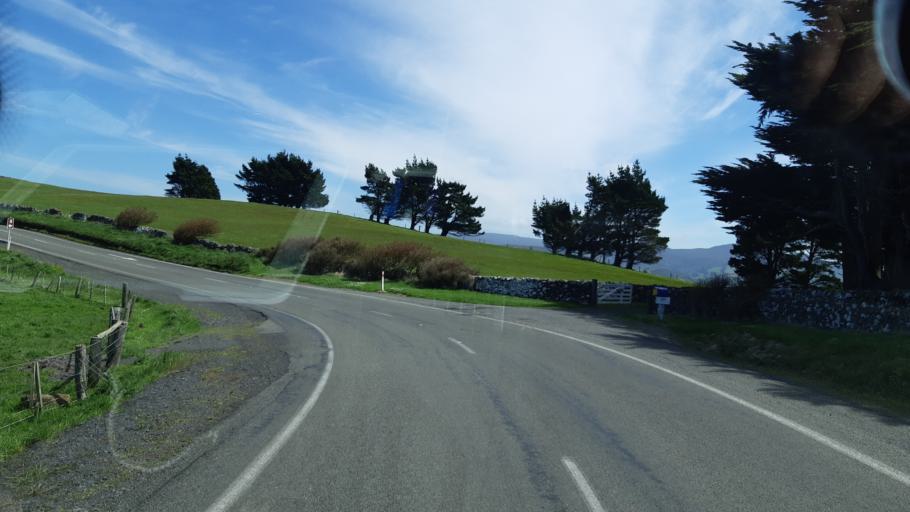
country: NZ
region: Otago
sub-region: Dunedin City
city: Portobello
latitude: -45.8825
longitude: 170.6049
